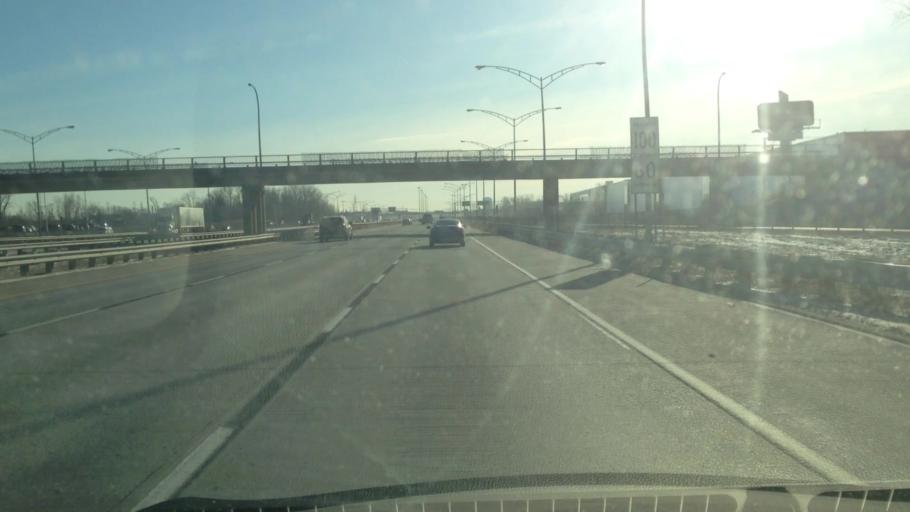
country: CA
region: Quebec
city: Dollard-Des Ormeaux
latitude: 45.5498
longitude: -73.8043
